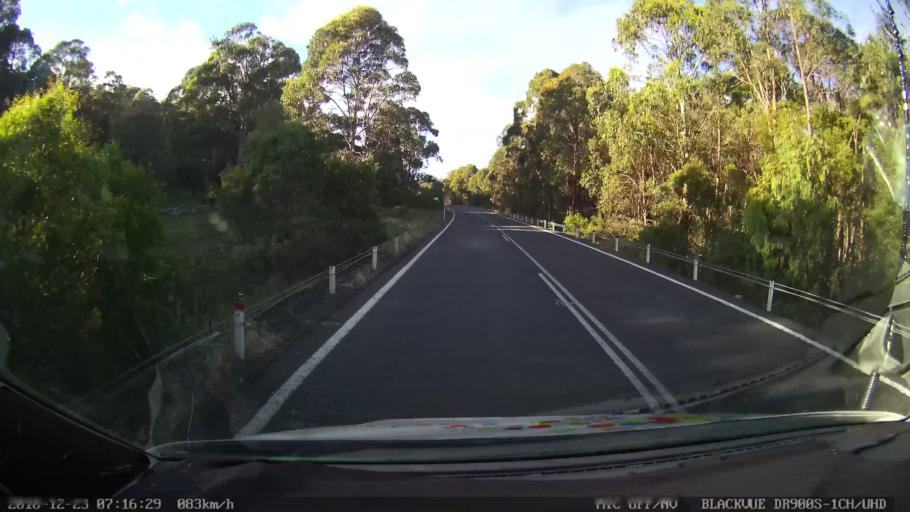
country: AU
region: New South Wales
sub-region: Bellingen
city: Dorrigo
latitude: -30.4563
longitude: 152.3091
